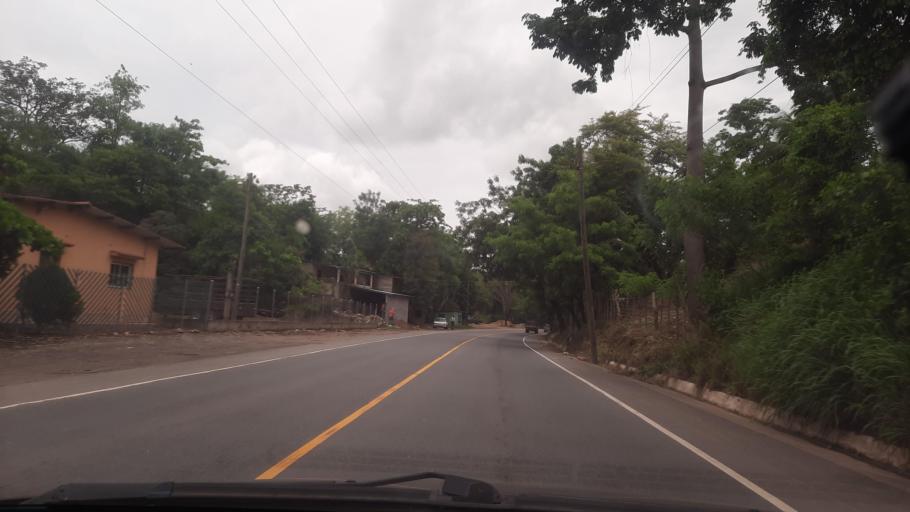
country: GT
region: Zacapa
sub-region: Municipio de Zacapa
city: Gualan
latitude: 15.1656
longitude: -89.3089
